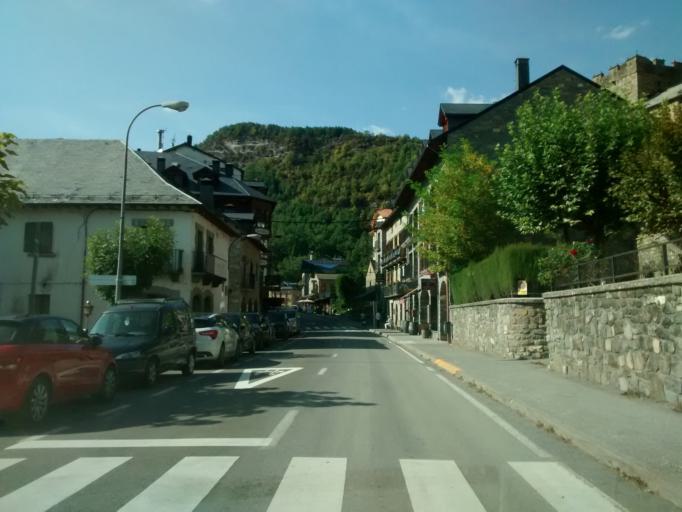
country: ES
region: Aragon
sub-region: Provincia de Huesca
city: Broto
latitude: 42.6035
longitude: -0.1218
